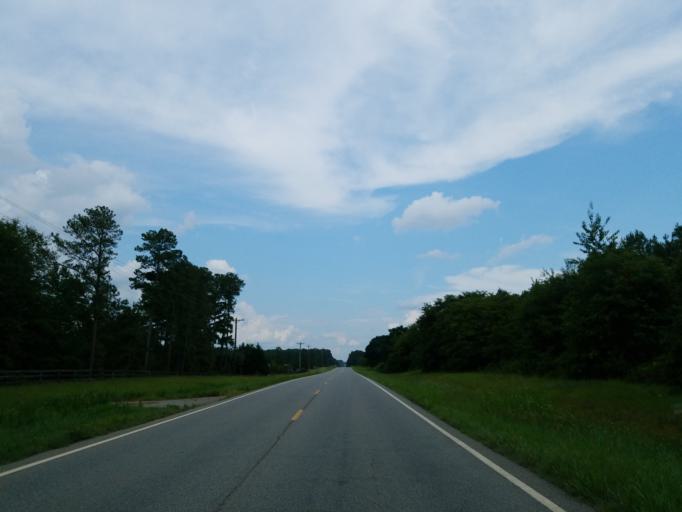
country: US
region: Georgia
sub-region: Dooly County
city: Unadilla
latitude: 32.3307
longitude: -83.7459
